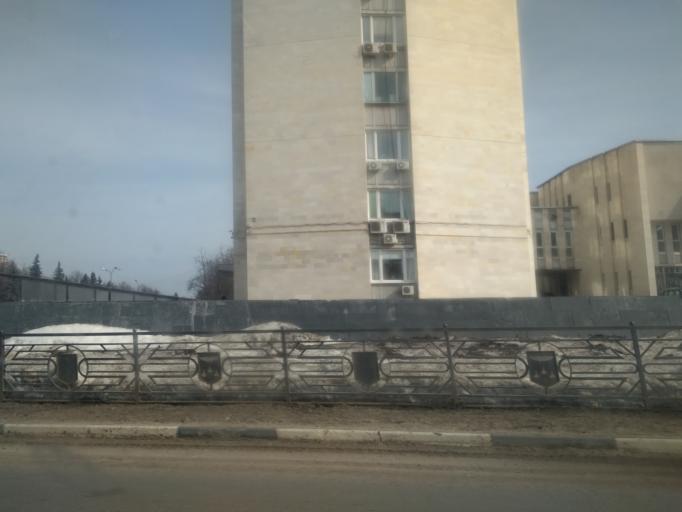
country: RU
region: Moskovskaya
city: Zhukovskiy
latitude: 55.5952
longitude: 38.1139
